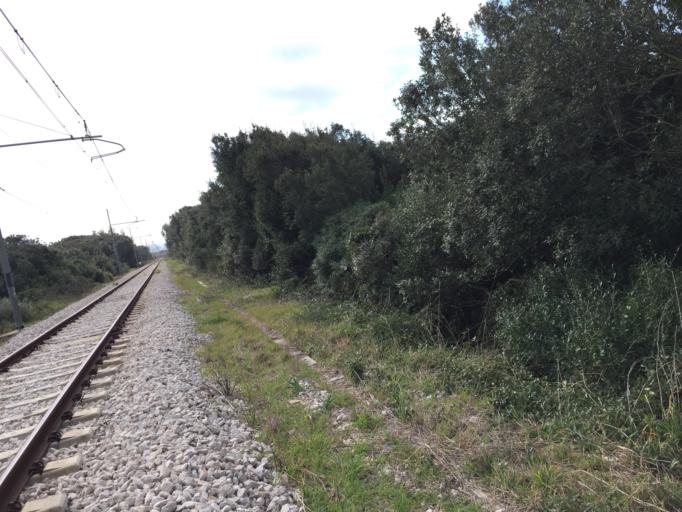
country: IT
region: Campania
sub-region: Provincia di Napoli
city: Monterusciello
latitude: 40.8466
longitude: 14.0493
